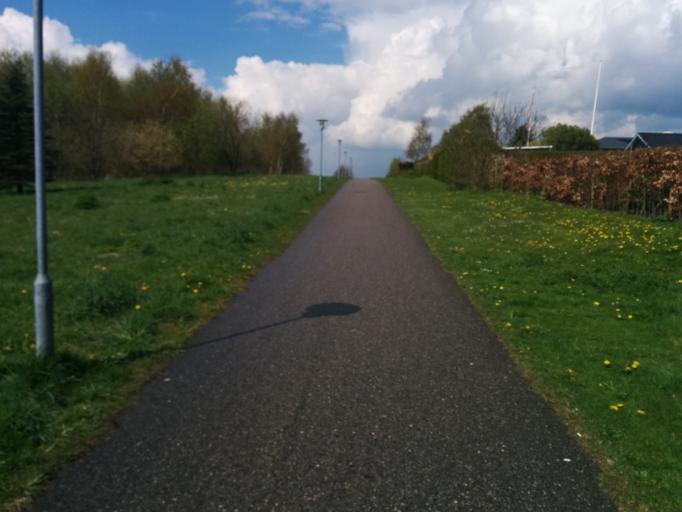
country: DK
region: Central Jutland
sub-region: Viborg Kommune
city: Viborg
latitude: 56.4461
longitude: 9.3740
